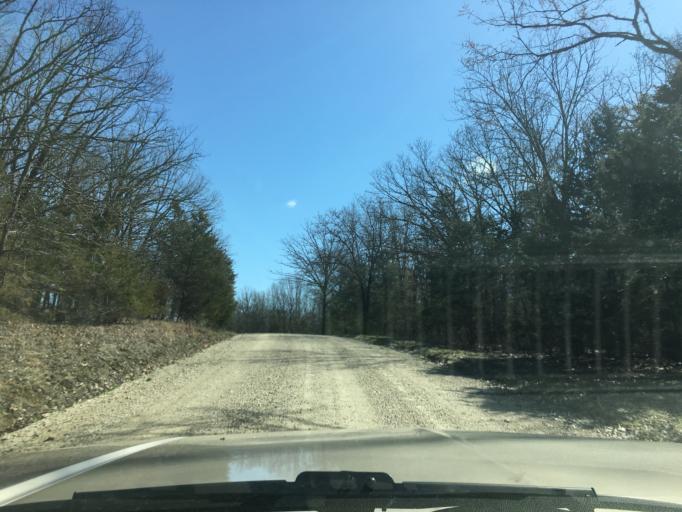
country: US
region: Missouri
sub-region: Franklin County
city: New Haven
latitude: 38.5523
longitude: -91.3217
